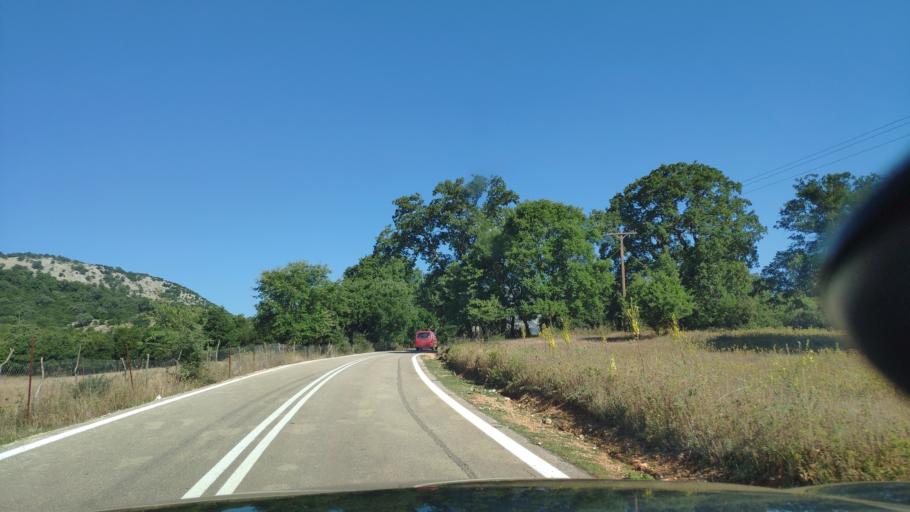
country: GR
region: West Greece
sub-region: Nomos Aitolias kai Akarnanias
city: Fitiai
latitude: 38.6857
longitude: 21.1193
